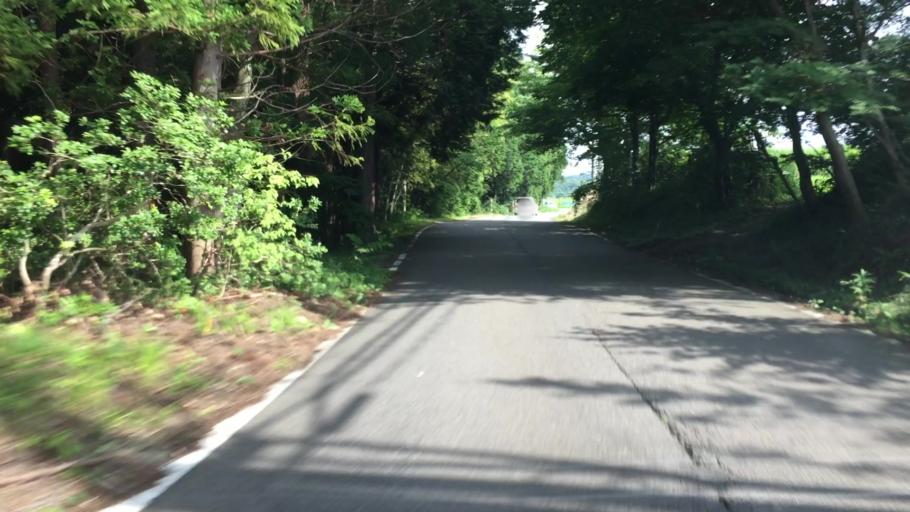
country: JP
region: Tochigi
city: Kuroiso
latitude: 37.0556
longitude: 139.9426
